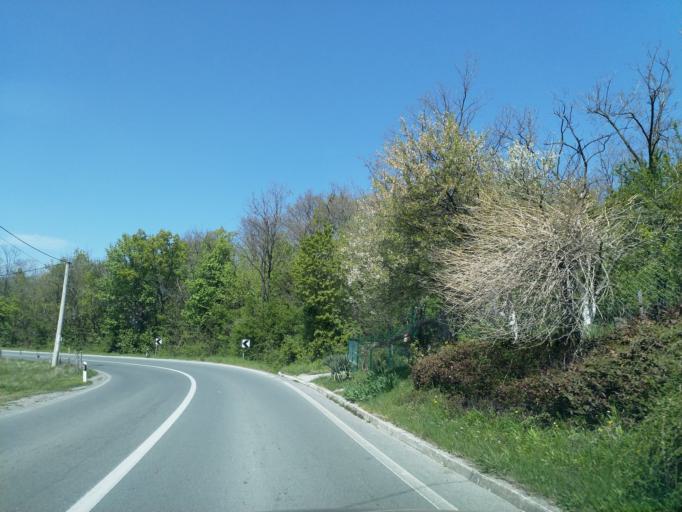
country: RS
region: Central Serbia
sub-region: Belgrade
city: Lazarevac
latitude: 44.3733
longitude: 20.3125
